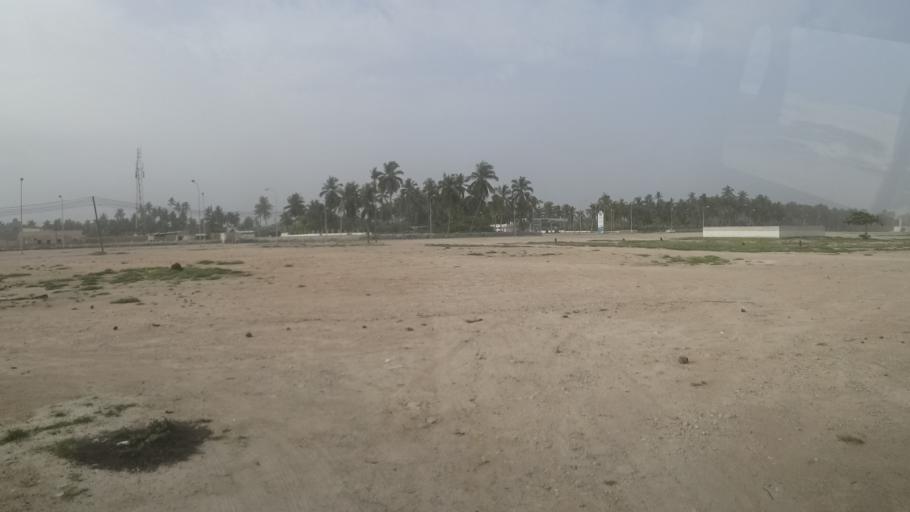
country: OM
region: Zufar
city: Salalah
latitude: 17.0019
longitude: 54.1123
